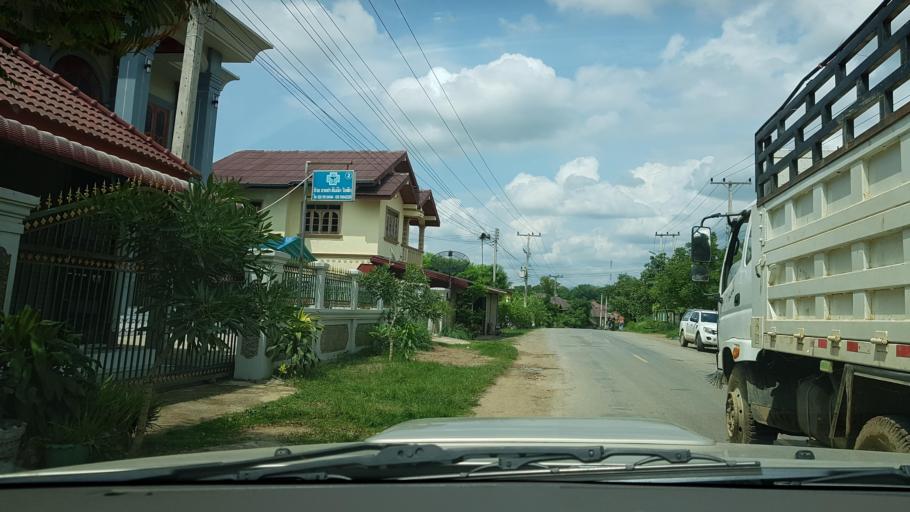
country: LA
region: Loungnamtha
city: Muang Nale
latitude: 20.1258
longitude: 101.4326
